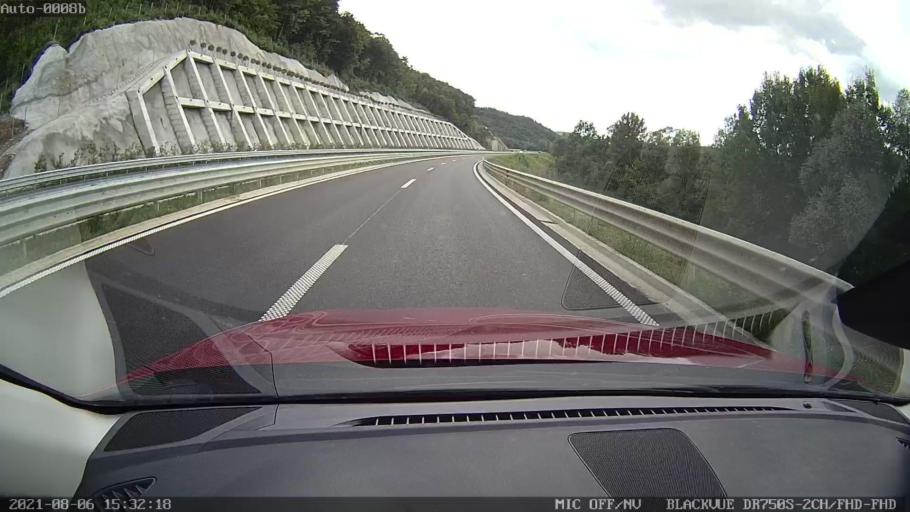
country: HR
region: Istarska
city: Pazin
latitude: 45.2664
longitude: 14.0125
